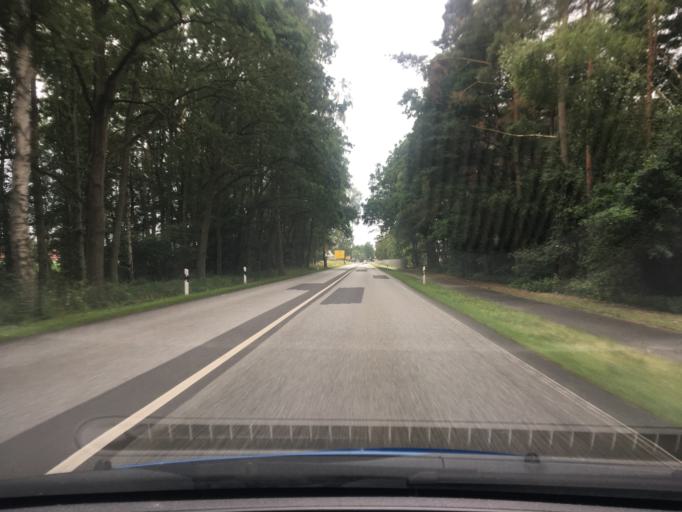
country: DE
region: Mecklenburg-Vorpommern
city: Stralendorf
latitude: 53.5168
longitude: 11.2986
